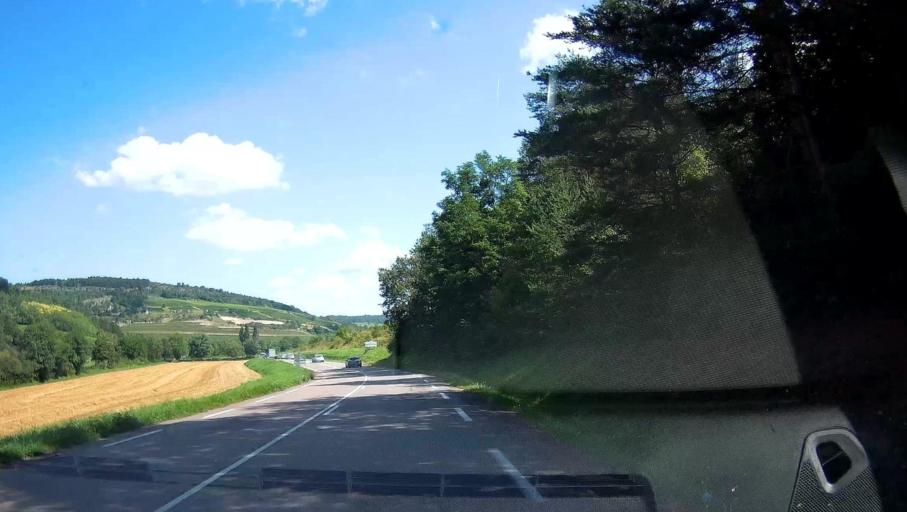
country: FR
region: Bourgogne
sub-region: Departement de la Cote-d'Or
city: Corpeau
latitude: 46.9733
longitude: 4.7007
